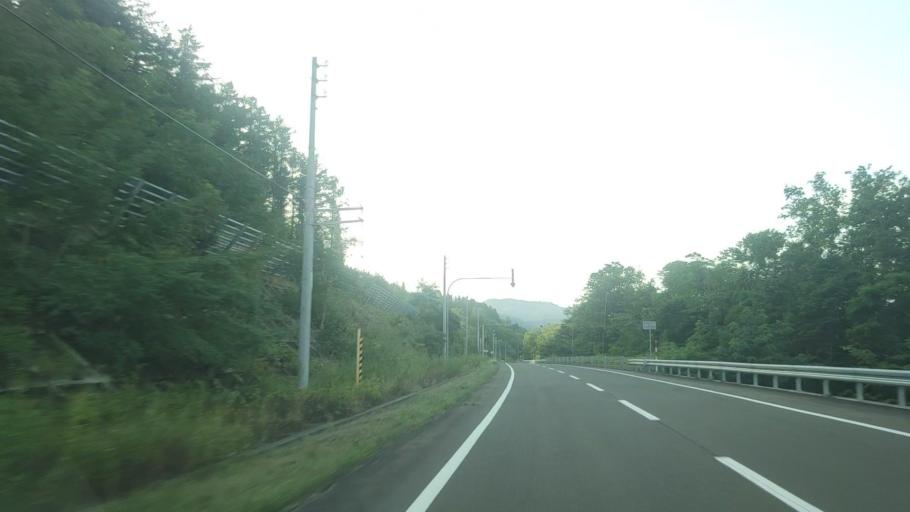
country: JP
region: Hokkaido
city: Bibai
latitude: 43.0713
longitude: 142.1041
